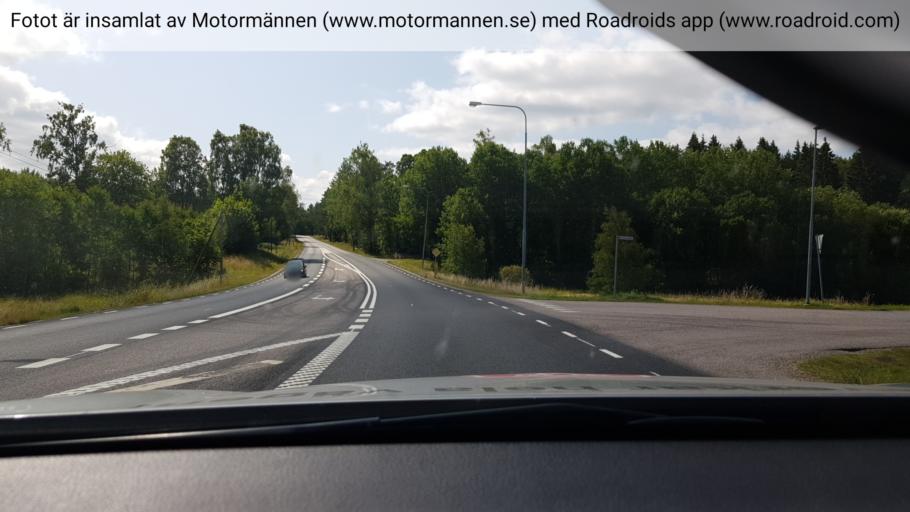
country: SE
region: Stockholm
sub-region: Osterakers Kommun
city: Akersberga
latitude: 59.5578
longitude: 18.2207
